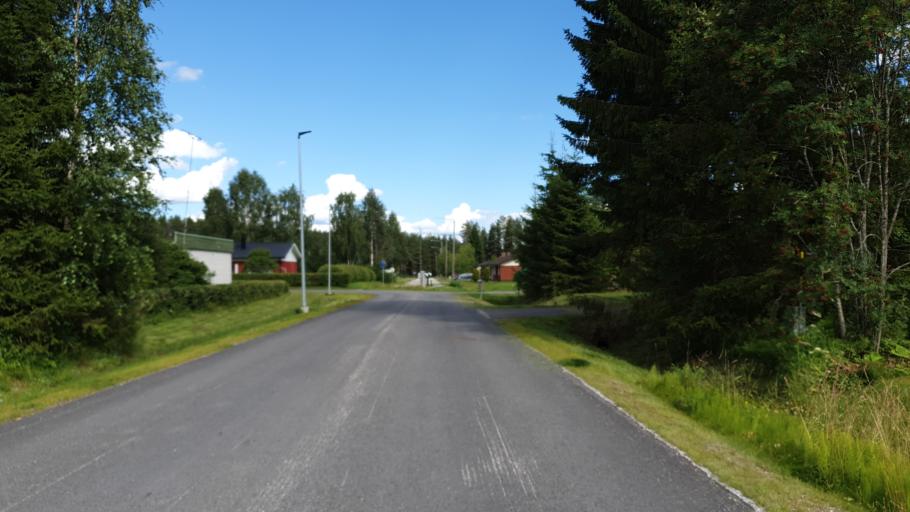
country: FI
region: Kainuu
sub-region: Kehys-Kainuu
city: Kuhmo
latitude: 64.1189
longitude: 29.5385
